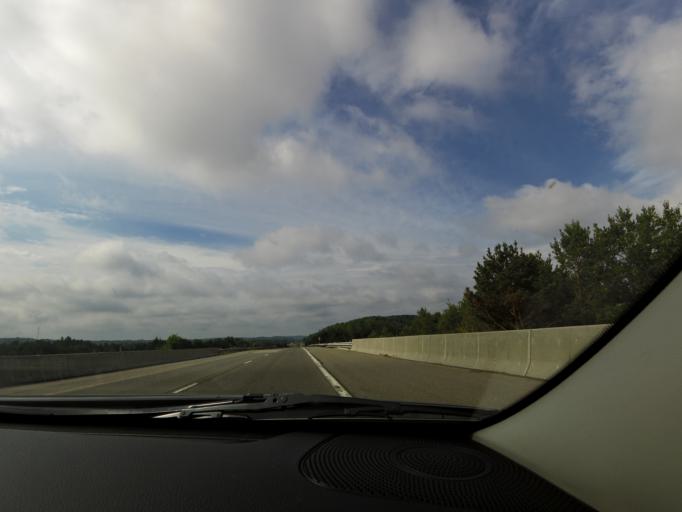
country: CA
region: Ontario
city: Huntsville
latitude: 45.3401
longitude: -79.2340
